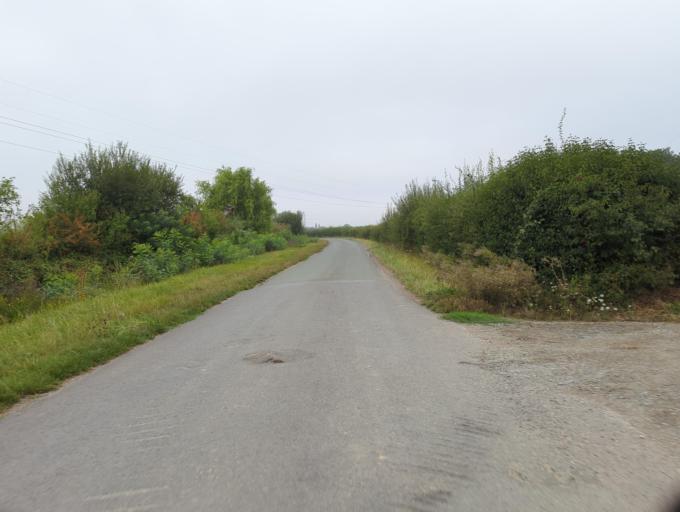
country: FR
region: Pays de la Loire
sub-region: Departement de Maine-et-Loire
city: Trelaze
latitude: 47.4794
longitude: -0.4661
